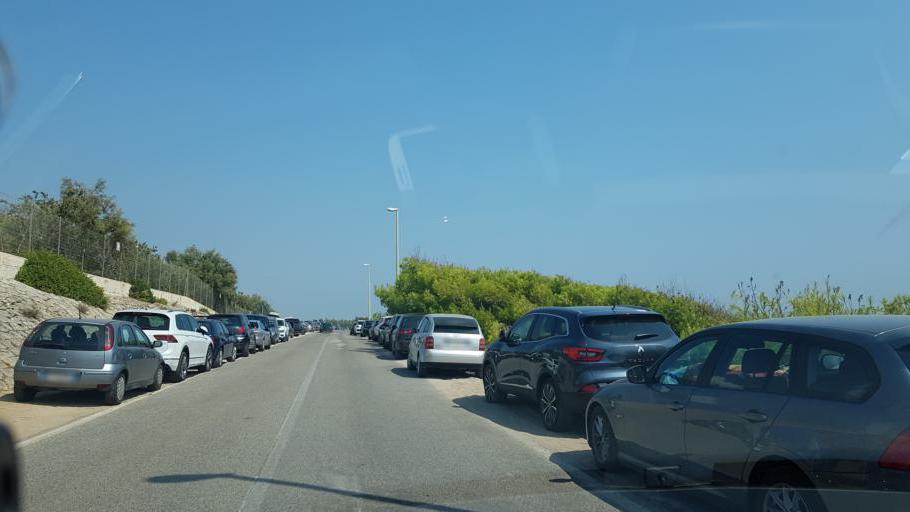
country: IT
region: Apulia
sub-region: Provincia di Taranto
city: Maruggio
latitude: 40.3002
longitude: 17.5771
